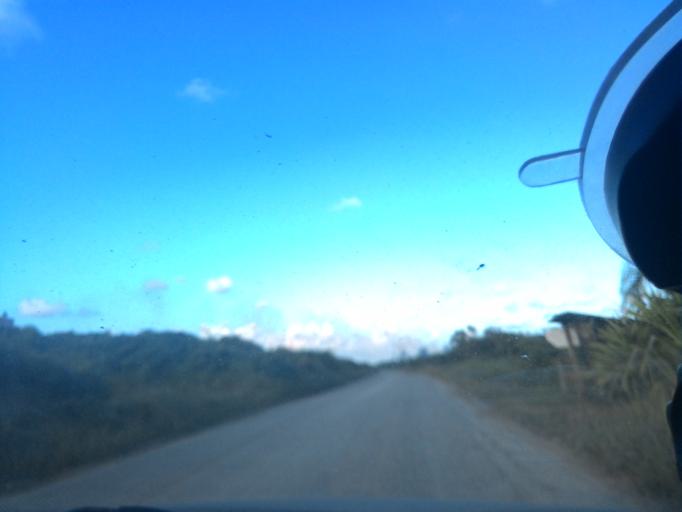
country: BR
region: Sao Paulo
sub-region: Iguape
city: Iguape
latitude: -24.8567
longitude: -47.7061
